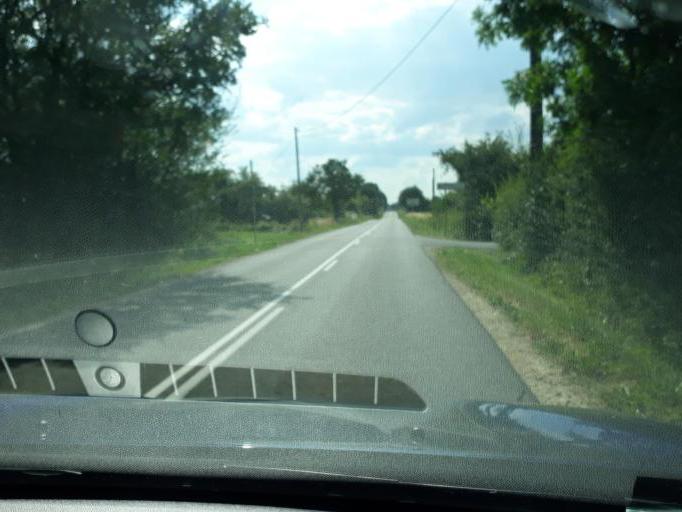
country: FR
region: Centre
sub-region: Departement du Cher
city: Nerondes
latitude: 47.0485
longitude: 2.8807
